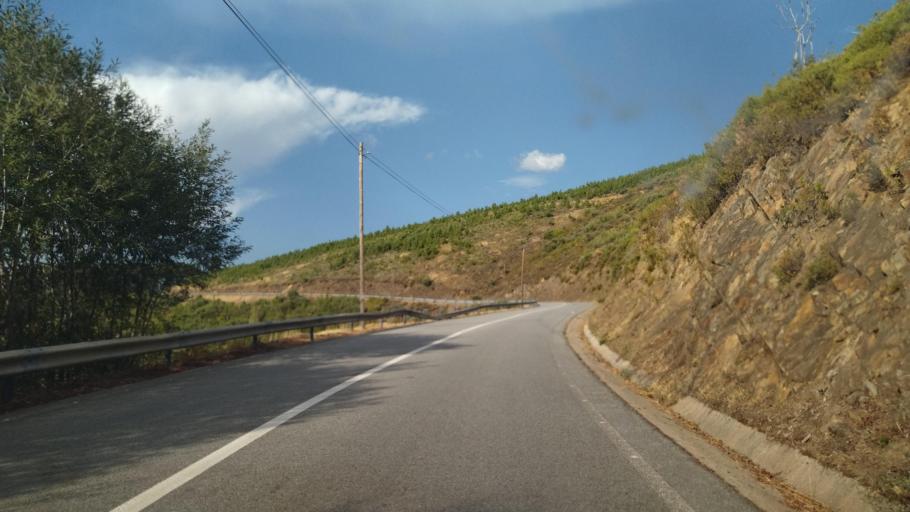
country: PT
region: Castelo Branco
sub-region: Covilha
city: Teixoso
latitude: 40.3698
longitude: -7.4480
